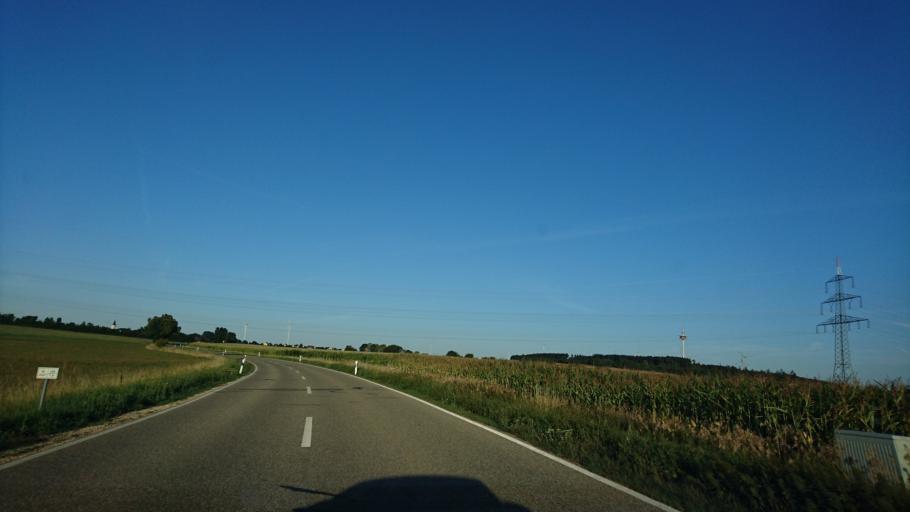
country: DE
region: Bavaria
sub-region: Regierungsbezirk Mittelfranken
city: Nennslingen
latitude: 49.0409
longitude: 11.1139
